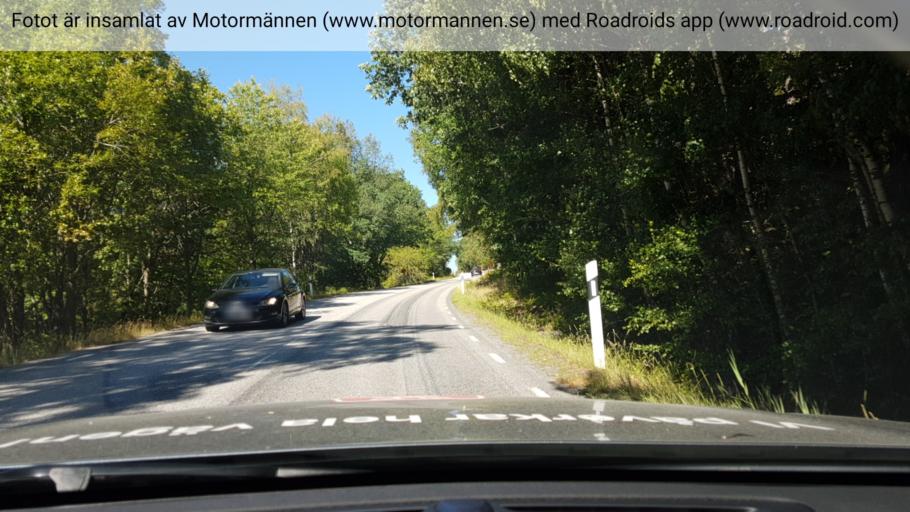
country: SE
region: Stockholm
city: Stenhamra
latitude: 59.2873
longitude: 17.7141
